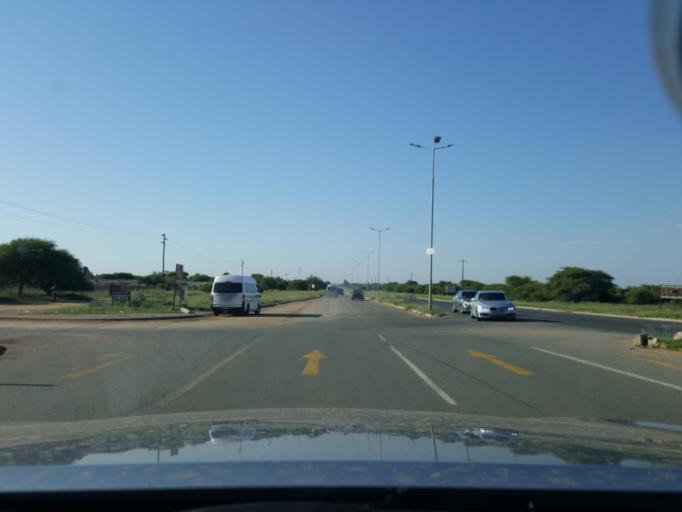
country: ZA
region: North-West
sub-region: Ngaka Modiri Molema District Municipality
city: Mmabatho
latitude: -25.7998
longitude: 25.6313
